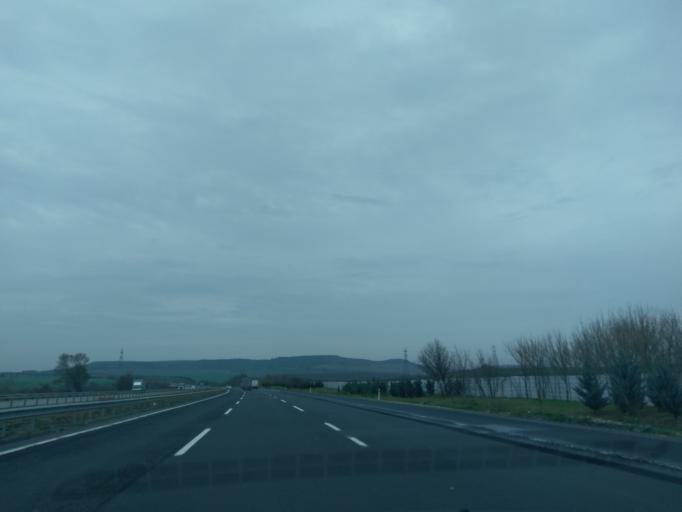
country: TR
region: Istanbul
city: Canta
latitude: 41.1480
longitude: 28.1464
